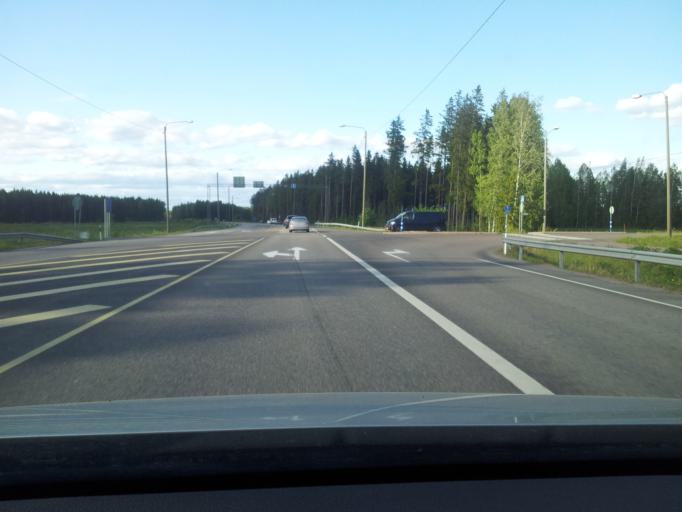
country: FI
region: Kymenlaakso
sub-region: Kouvola
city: Elimaeki
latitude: 60.8261
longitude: 26.5365
